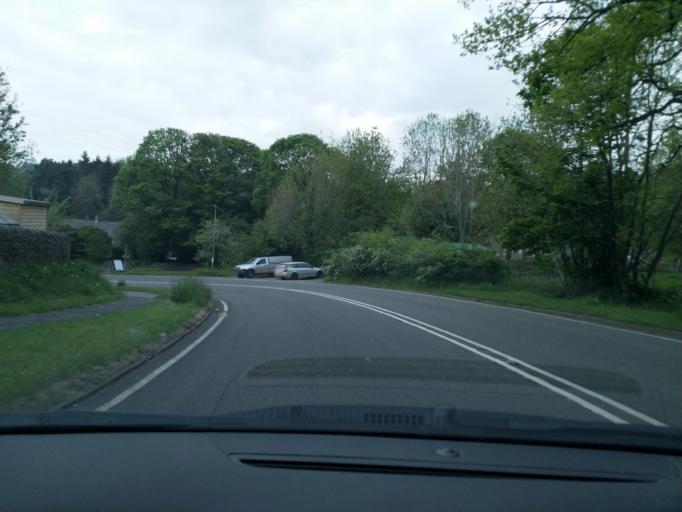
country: GB
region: England
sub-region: Derbyshire
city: Hathersage
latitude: 53.3303
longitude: -1.6502
